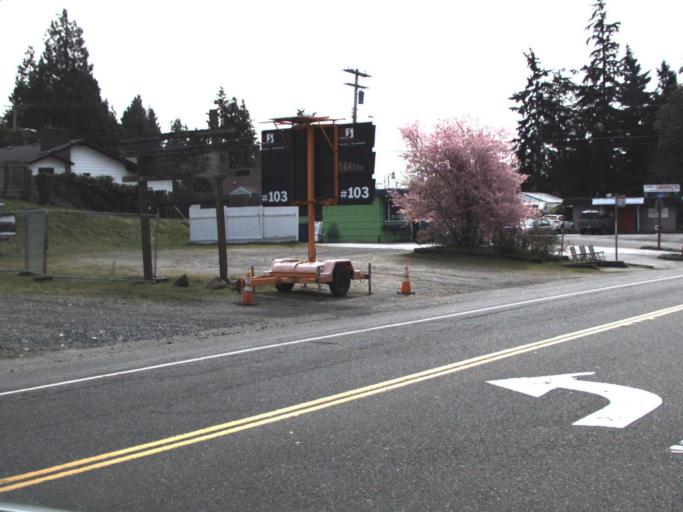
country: US
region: Washington
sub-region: King County
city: Des Moines
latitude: 47.4166
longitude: -122.3353
